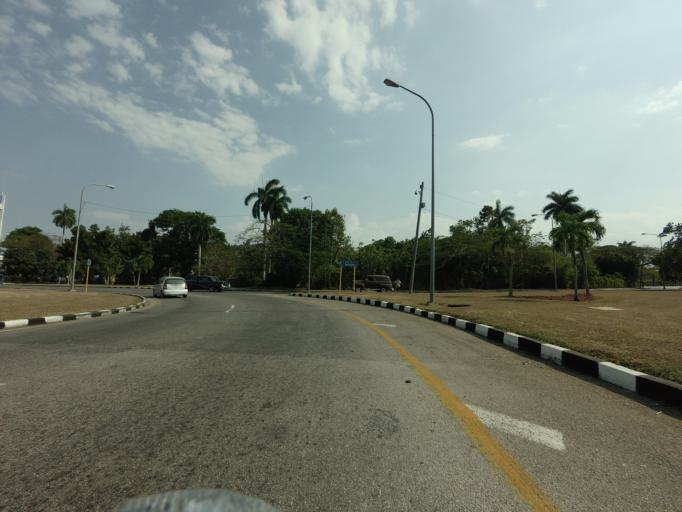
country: CU
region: La Habana
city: Cerro
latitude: 23.0759
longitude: -82.4573
